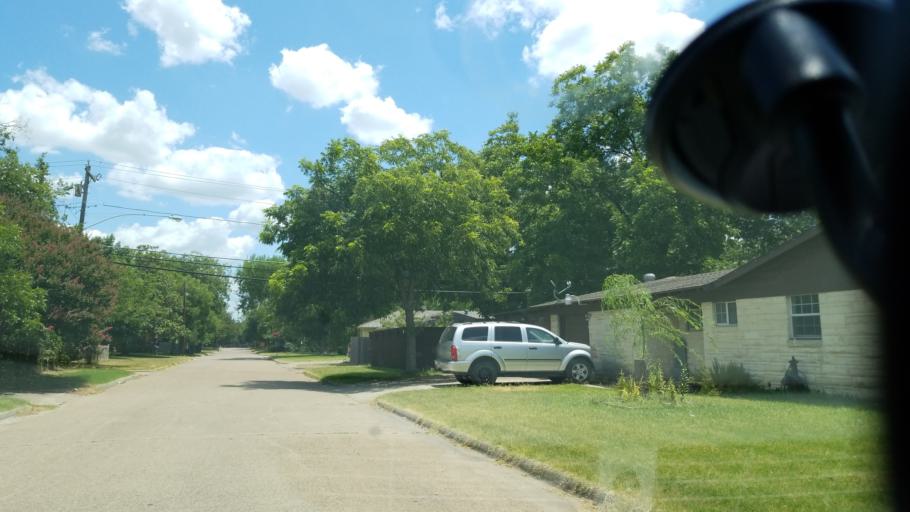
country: US
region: Texas
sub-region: Dallas County
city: Cockrell Hill
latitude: 32.7112
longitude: -96.8484
